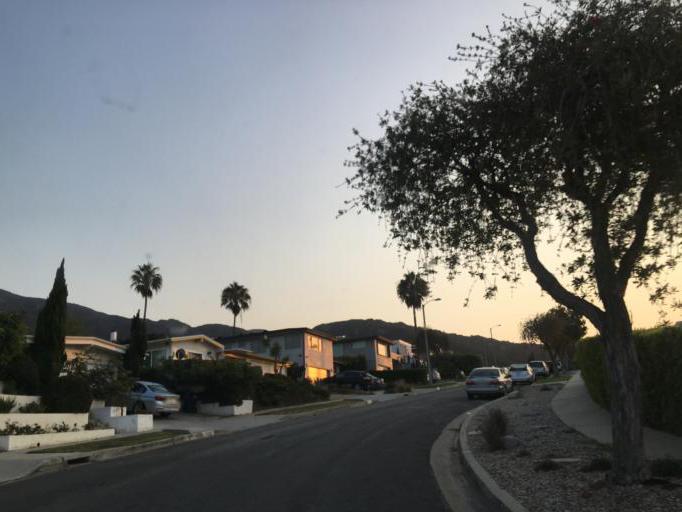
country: US
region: California
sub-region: Los Angeles County
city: Topanga
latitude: 34.0455
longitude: -118.5732
